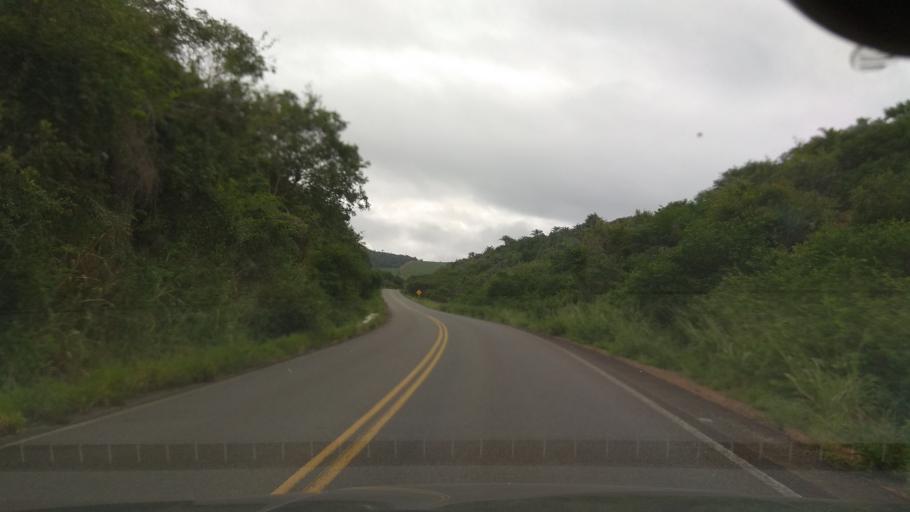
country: BR
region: Bahia
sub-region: Santa Ines
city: Santa Ines
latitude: -13.2584
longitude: -39.7832
